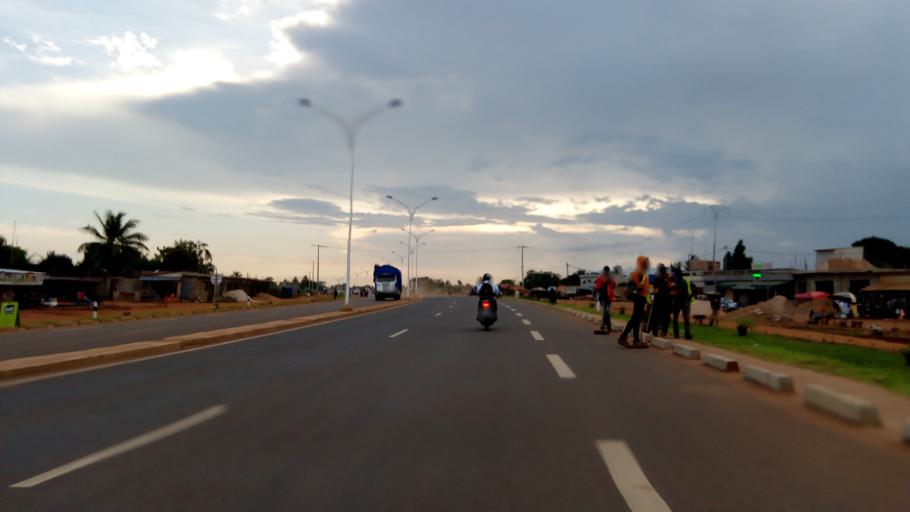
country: TG
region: Maritime
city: Lome
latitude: 6.2673
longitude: 1.1505
